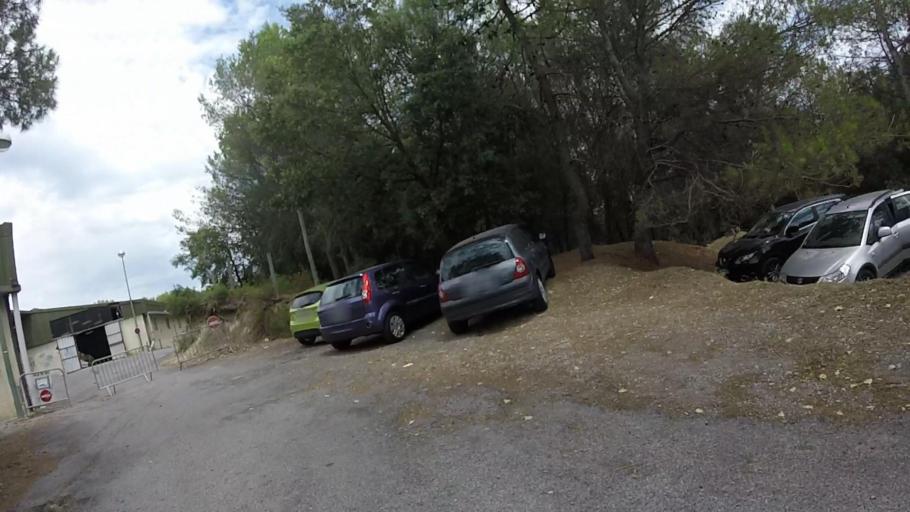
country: FR
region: Provence-Alpes-Cote d'Azur
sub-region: Departement des Alpes-Maritimes
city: Biot
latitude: 43.6214
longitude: 7.0647
